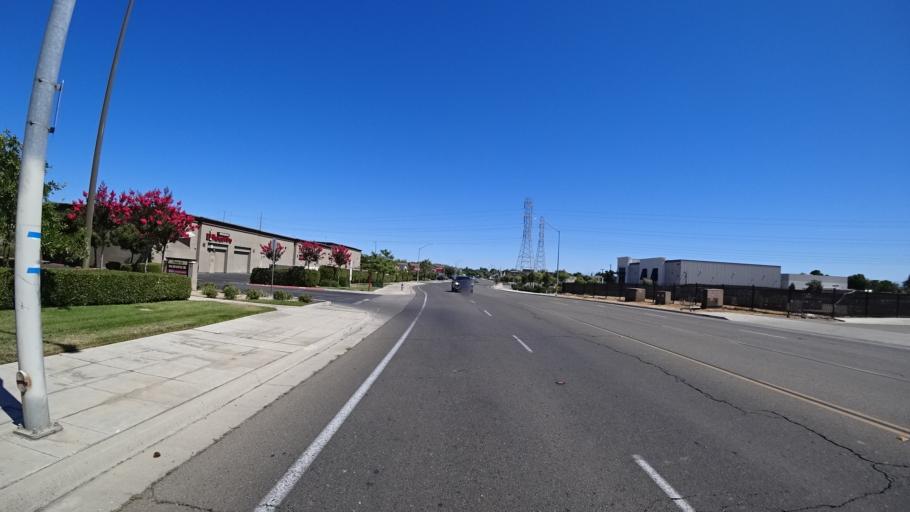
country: US
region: California
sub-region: Fresno County
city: West Park
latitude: 36.8060
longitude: -119.8582
